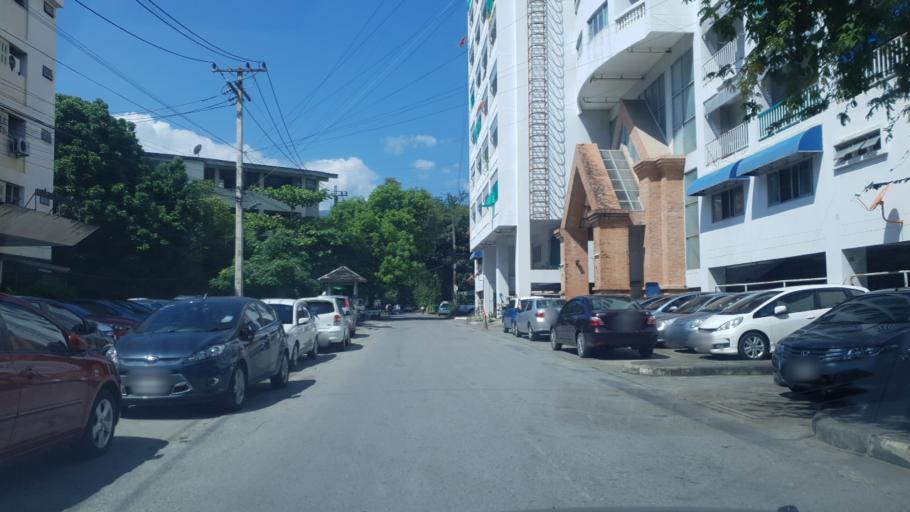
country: TH
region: Chiang Mai
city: Chiang Mai
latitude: 18.7920
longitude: 98.9732
